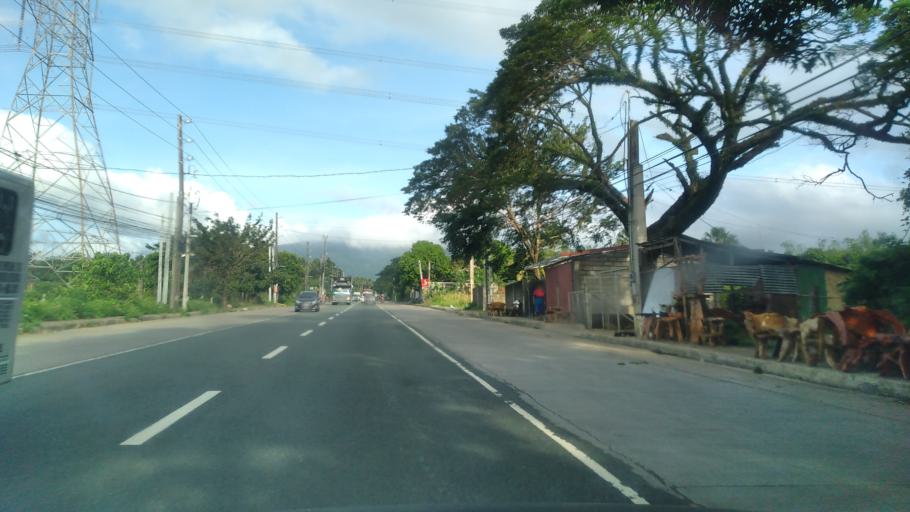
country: PH
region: Calabarzon
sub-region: Province of Quezon
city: Isabang
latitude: 13.9717
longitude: 121.5607
